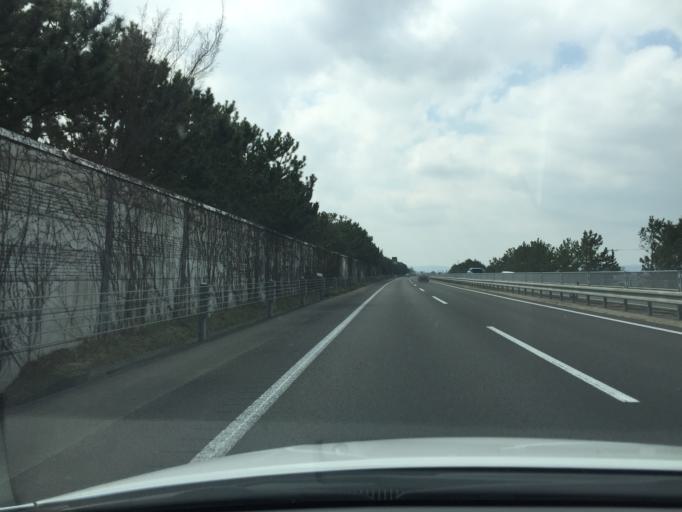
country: JP
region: Miyagi
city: Iwanuma
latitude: 38.1726
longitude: 140.9220
